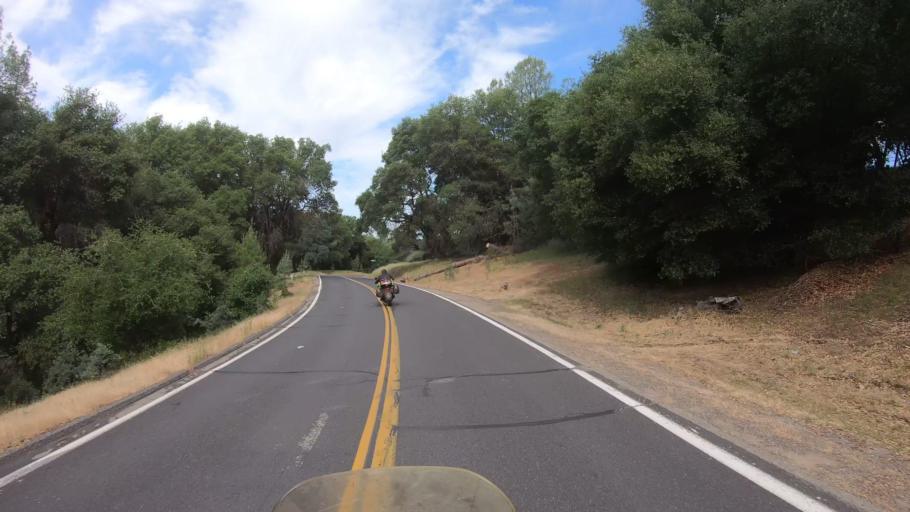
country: US
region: California
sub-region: Tuolumne County
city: Tuolumne City
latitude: 37.8574
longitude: -120.1732
